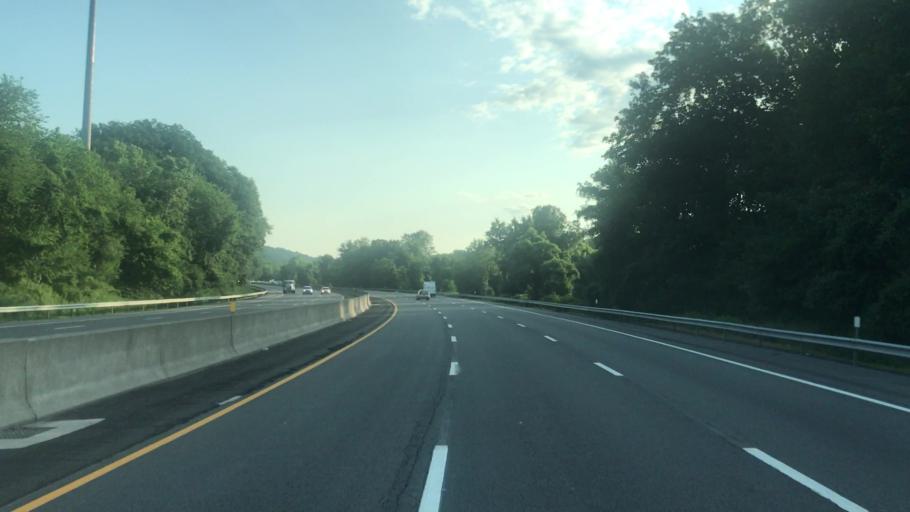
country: US
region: New York
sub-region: Westchester County
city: Ardsley
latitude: 41.0140
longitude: -73.8476
